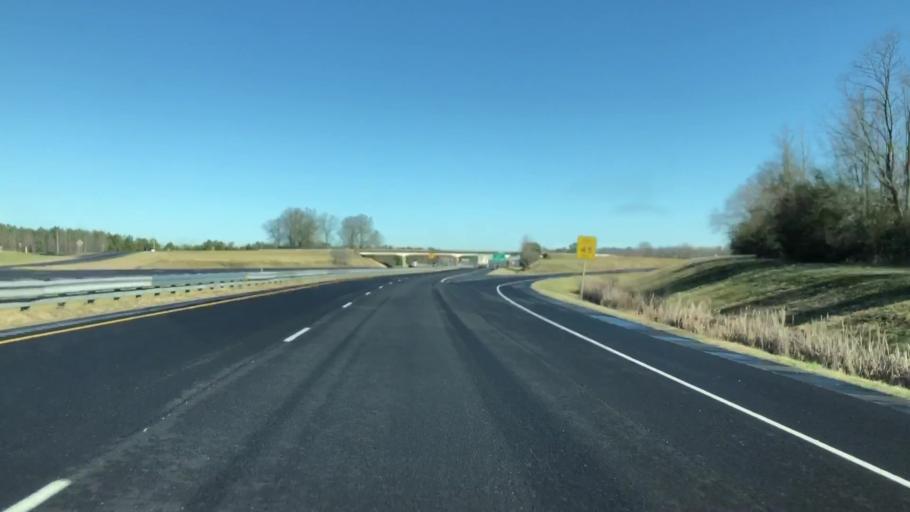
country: US
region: Alabama
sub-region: Limestone County
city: Ardmore
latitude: 34.9171
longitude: -86.9081
